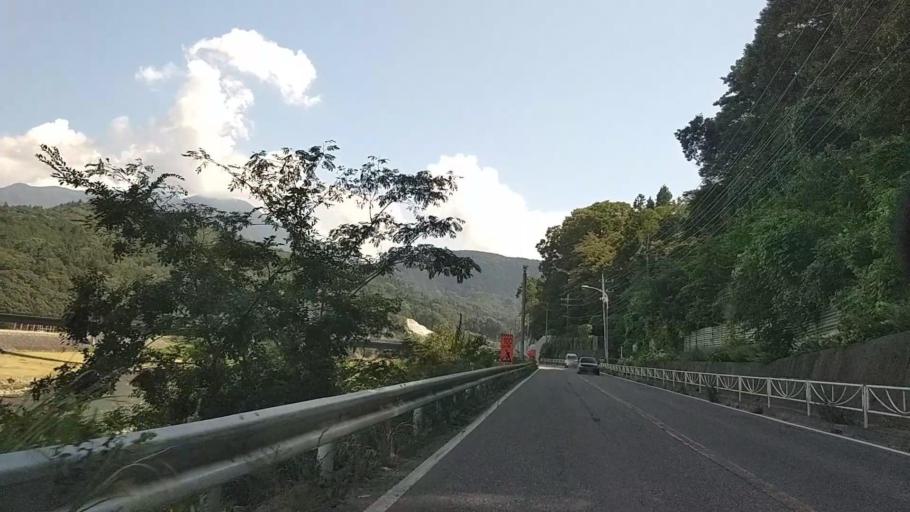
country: JP
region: Yamanashi
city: Ryuo
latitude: 35.4585
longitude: 138.4430
